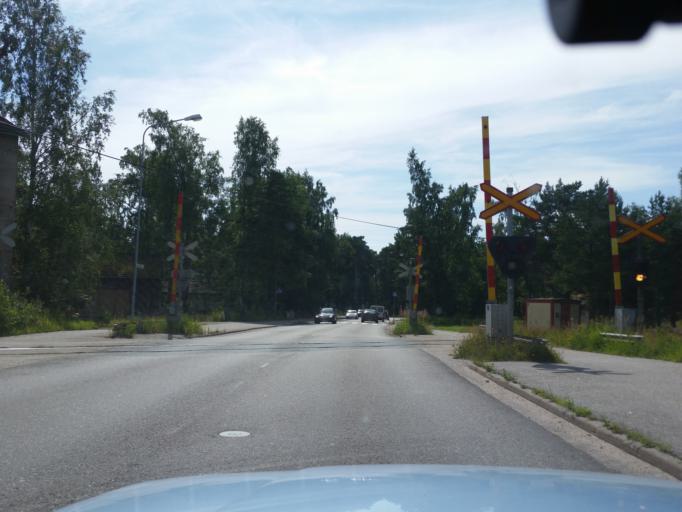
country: FI
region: Uusimaa
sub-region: Raaseporin
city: Hanko
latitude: 59.8308
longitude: 22.9897
